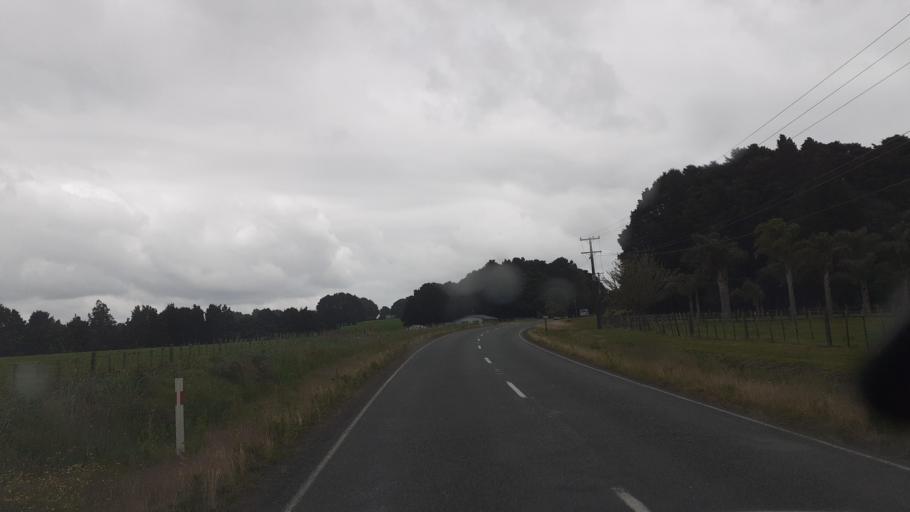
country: NZ
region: Northland
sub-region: Far North District
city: Waimate North
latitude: -35.2899
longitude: 173.8257
